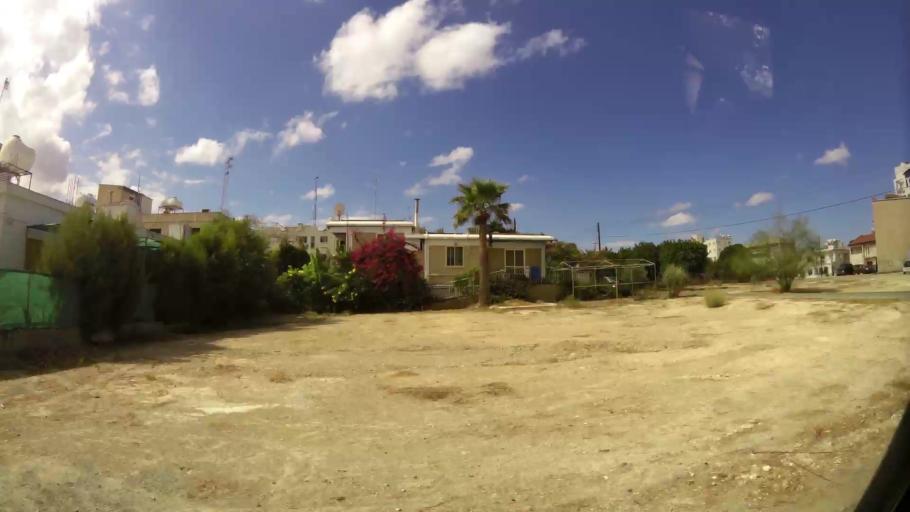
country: CY
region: Lefkosia
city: Nicosia
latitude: 35.1513
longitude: 33.3648
